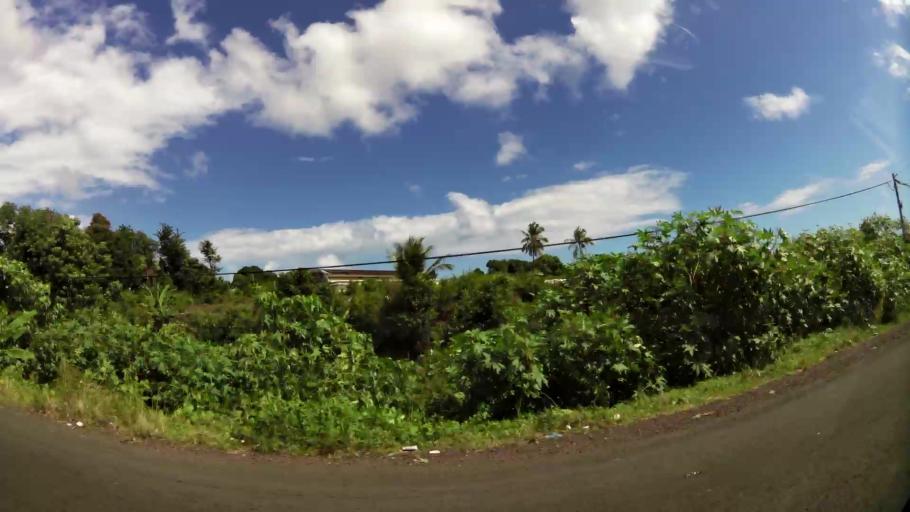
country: KM
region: Grande Comore
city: Mavingouni
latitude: -11.7303
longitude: 43.2497
